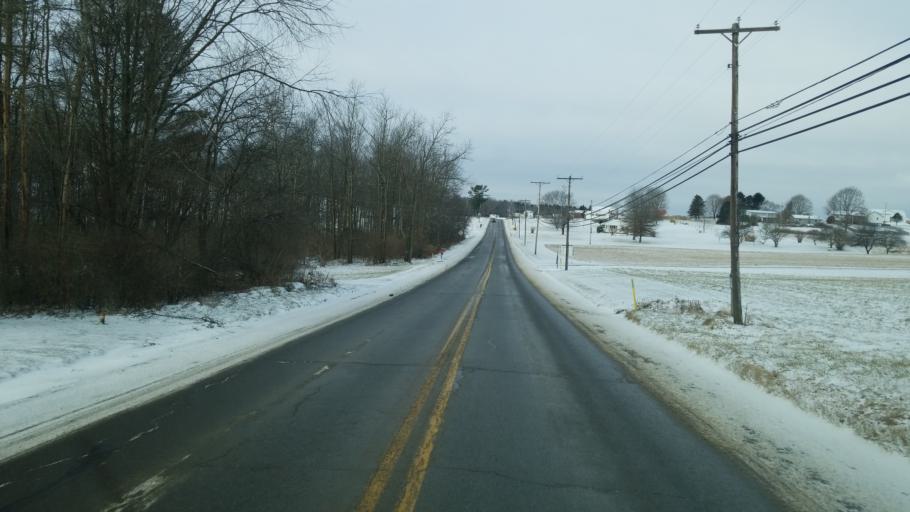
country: US
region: Pennsylvania
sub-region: Clarion County
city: Knox
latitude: 41.2343
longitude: -79.5641
